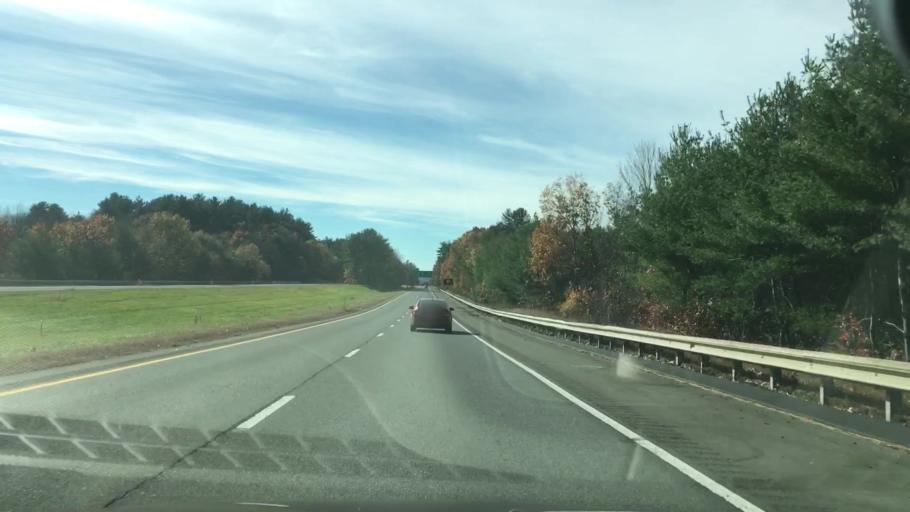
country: US
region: Massachusetts
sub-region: Franklin County
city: Bernardston
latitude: 42.6465
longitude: -72.5651
